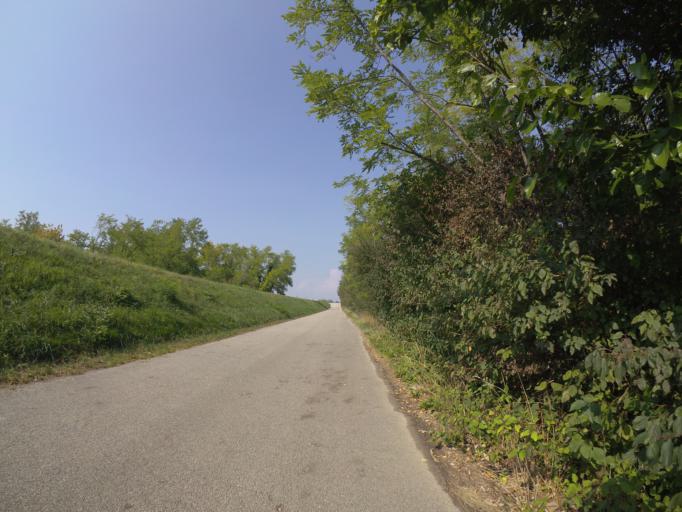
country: IT
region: Friuli Venezia Giulia
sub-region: Provincia di Udine
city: Camino al Tagliamento
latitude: 45.9491
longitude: 12.9159
